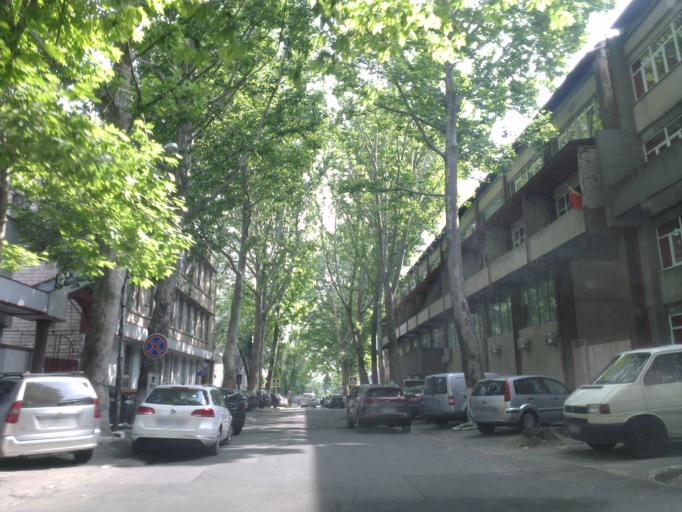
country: MD
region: Chisinau
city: Chisinau
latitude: 47.0313
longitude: 28.8238
